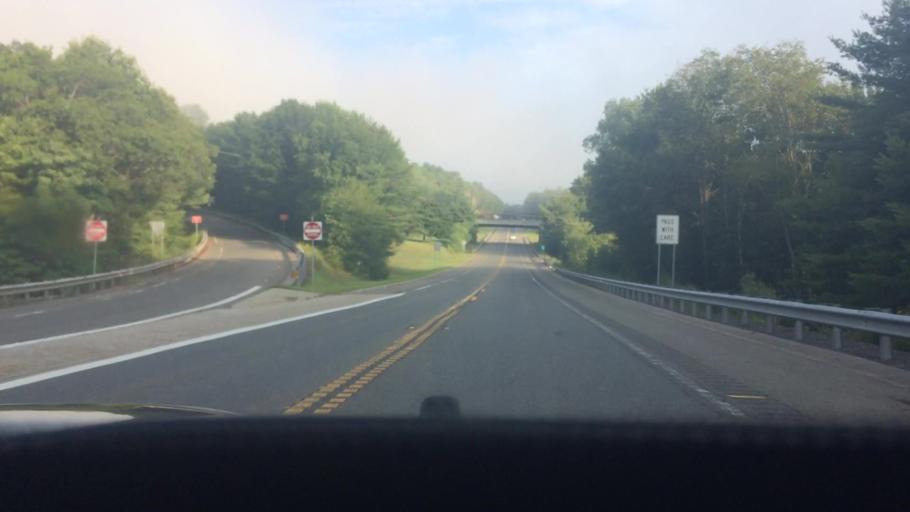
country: US
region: Massachusetts
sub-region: Franklin County
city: Orange
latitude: 42.5905
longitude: -72.3324
